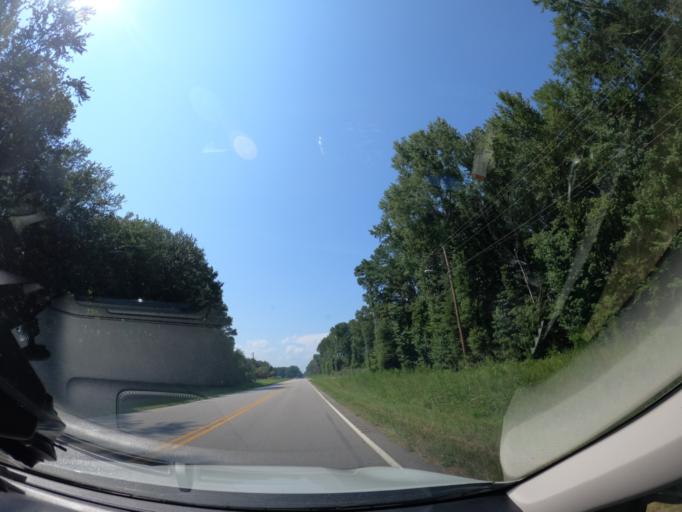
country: US
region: South Carolina
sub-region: Richland County
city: Hopkins
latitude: 33.8844
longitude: -80.9080
